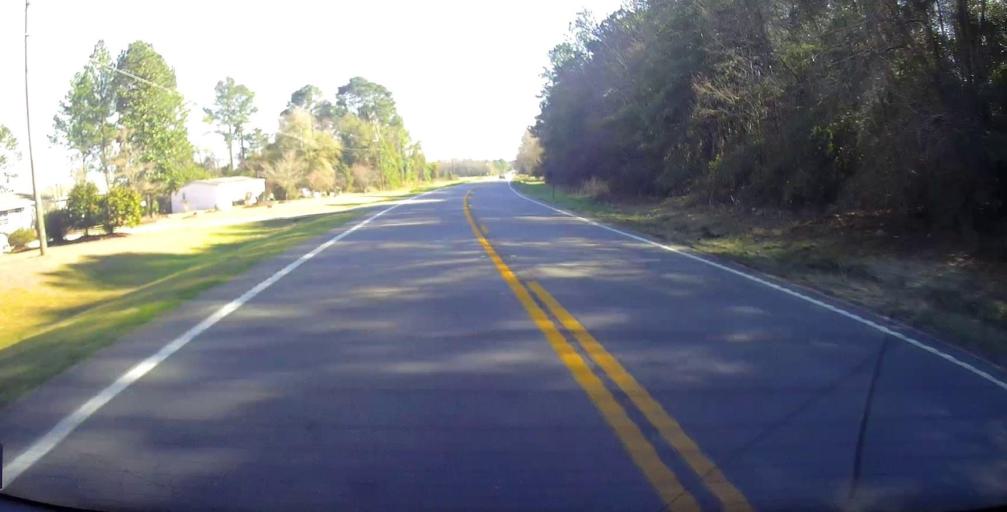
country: US
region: Georgia
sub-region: Macon County
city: Oglethorpe
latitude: 32.3270
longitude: -84.0717
